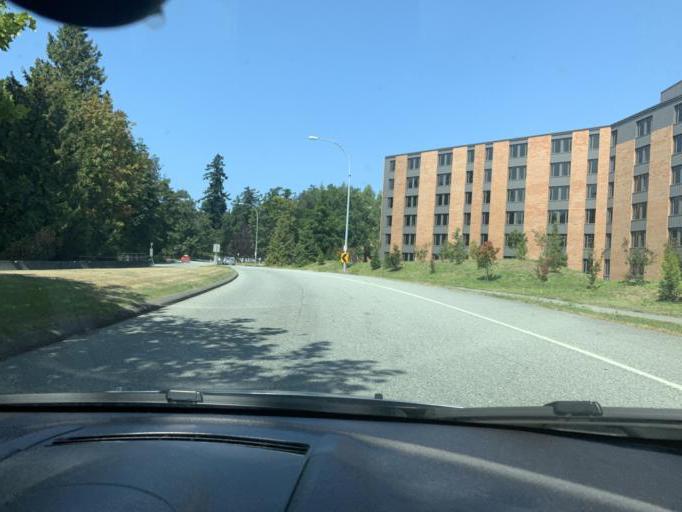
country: CA
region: British Columbia
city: West End
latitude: 49.2563
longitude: -123.2518
